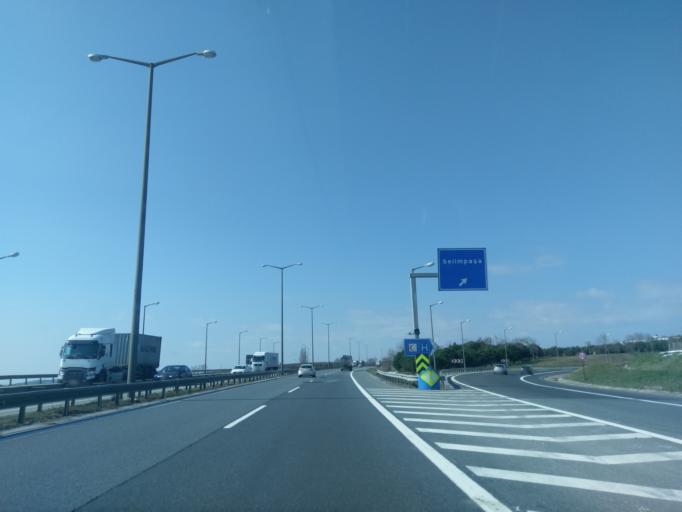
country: TR
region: Istanbul
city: Selimpasa
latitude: 41.0684
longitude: 28.3885
